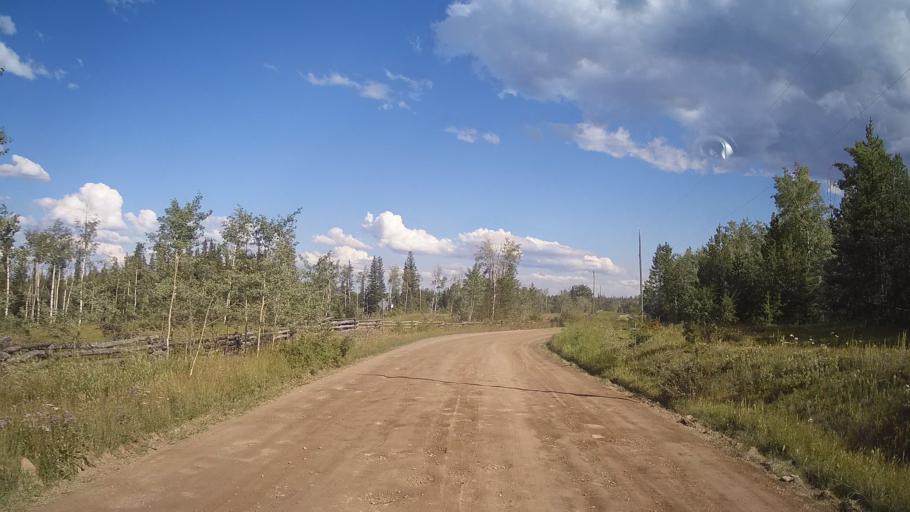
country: CA
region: British Columbia
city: Cache Creek
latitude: 51.2651
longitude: -121.6986
